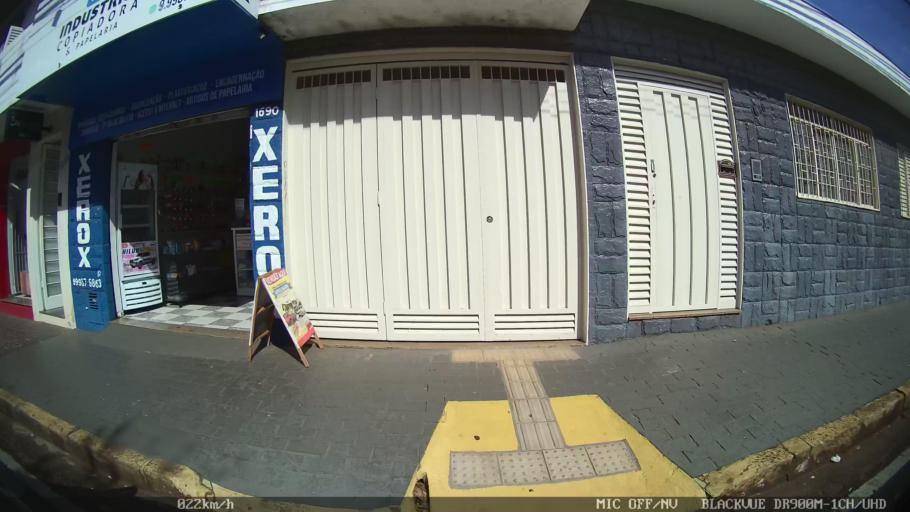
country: BR
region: Sao Paulo
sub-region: Franca
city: Franca
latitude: -20.5362
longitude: -47.3988
